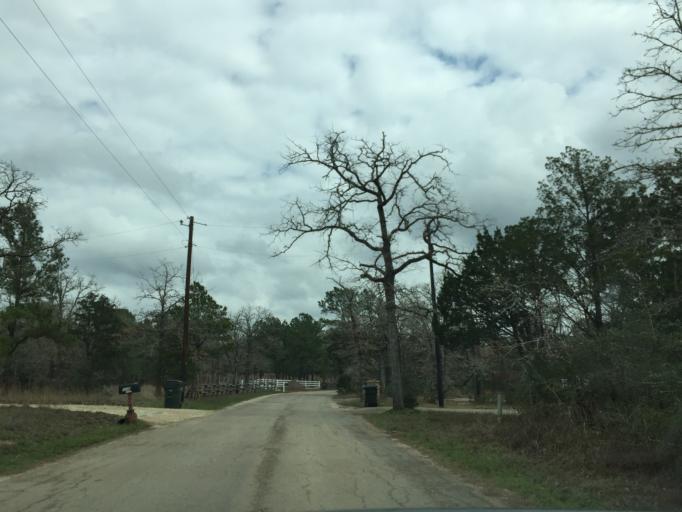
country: US
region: Texas
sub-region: Bastrop County
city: Bastrop
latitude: 30.1276
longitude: -97.2894
